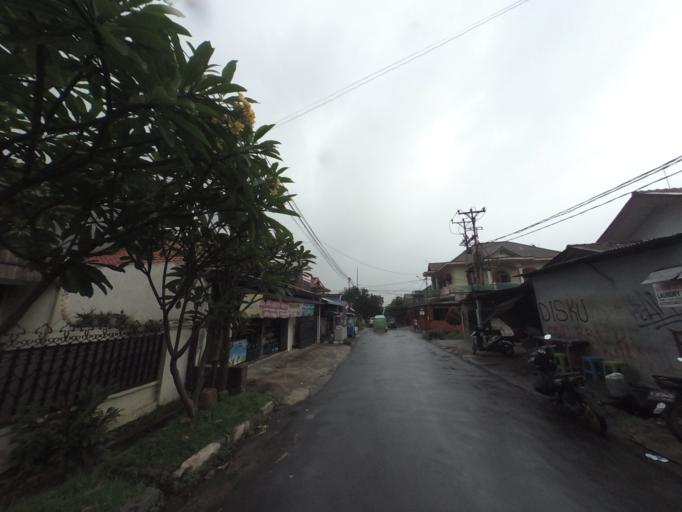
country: ID
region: West Java
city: Bogor
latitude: -6.5697
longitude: 106.7935
